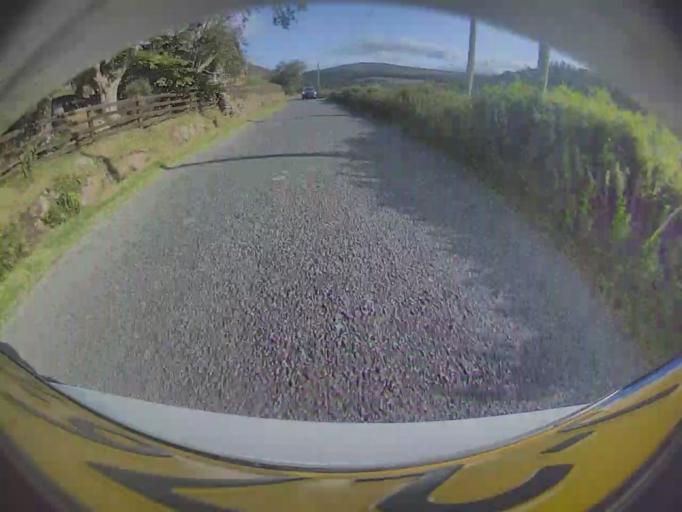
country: IE
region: Leinster
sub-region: Wicklow
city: Rathdrum
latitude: 53.0469
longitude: -6.3283
